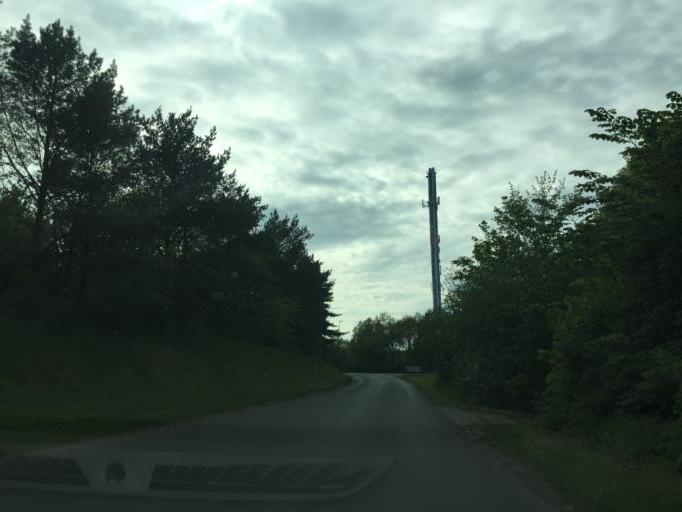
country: DK
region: South Denmark
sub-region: Odense Kommune
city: Hojby
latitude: 55.3400
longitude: 10.4440
